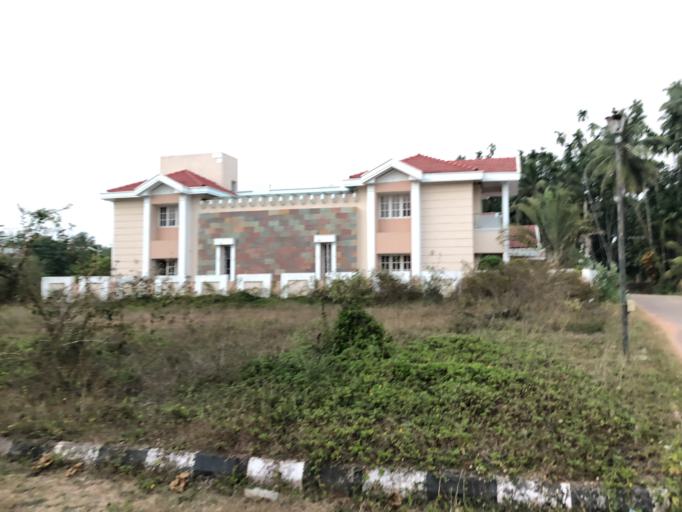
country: IN
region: Karnataka
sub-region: Dakshina Kannada
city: Mangalore
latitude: 12.8908
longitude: 74.8647
